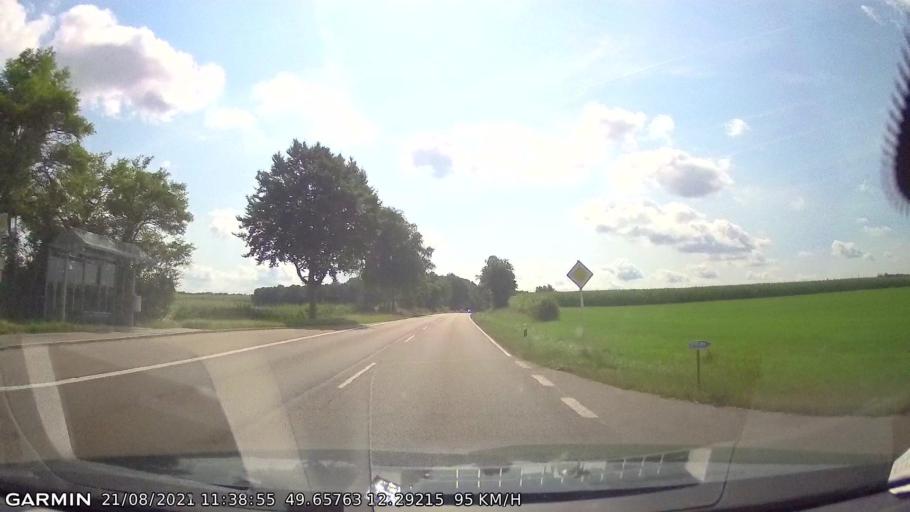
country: DE
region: Bavaria
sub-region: Upper Palatinate
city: Waldthurn
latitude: 49.6575
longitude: 12.2923
